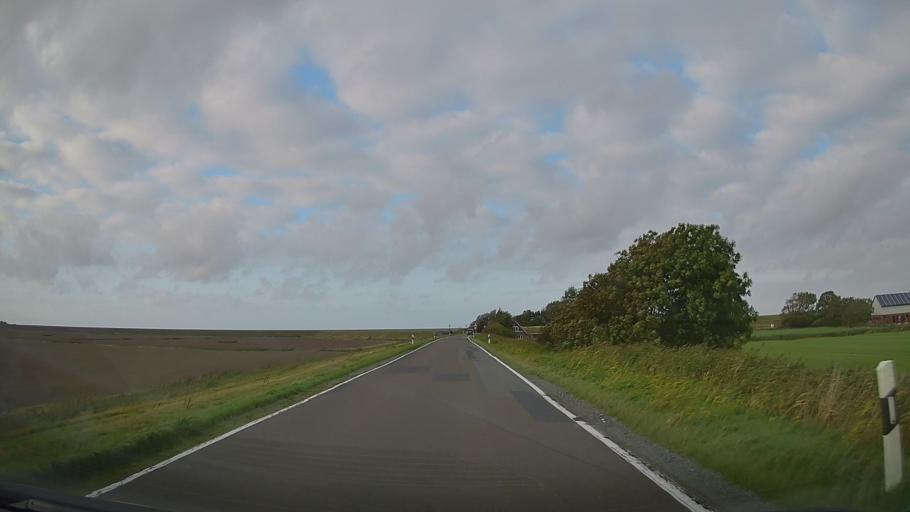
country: DE
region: Schleswig-Holstein
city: Osterhever
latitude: 54.3892
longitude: 8.7580
